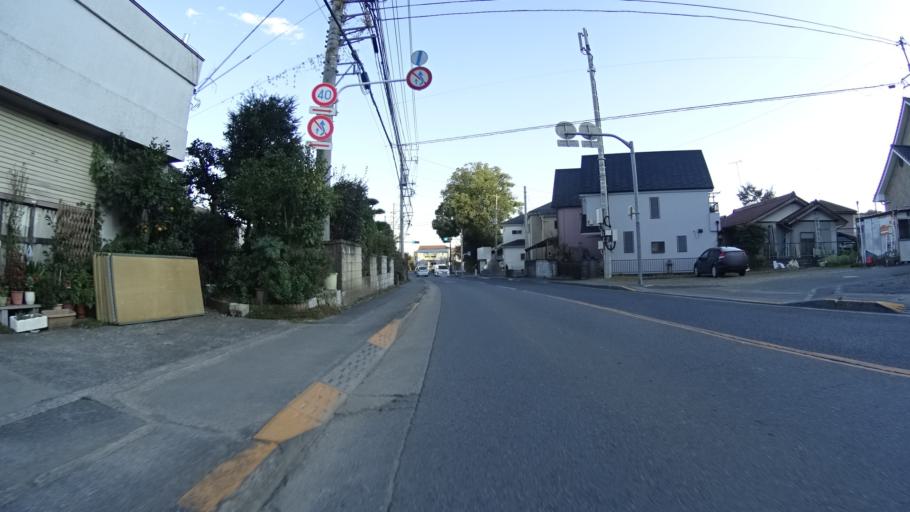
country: JP
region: Tokyo
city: Hachioji
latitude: 35.6811
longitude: 139.2777
